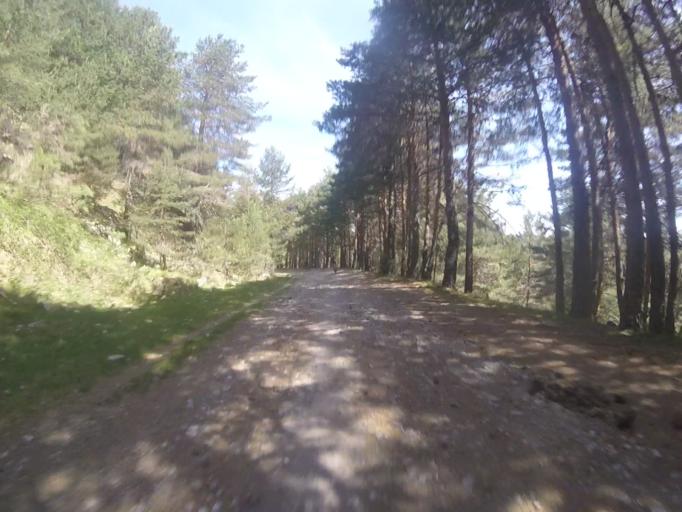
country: ES
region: Madrid
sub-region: Provincia de Madrid
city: Cercedilla
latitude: 40.8086
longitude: -4.0556
